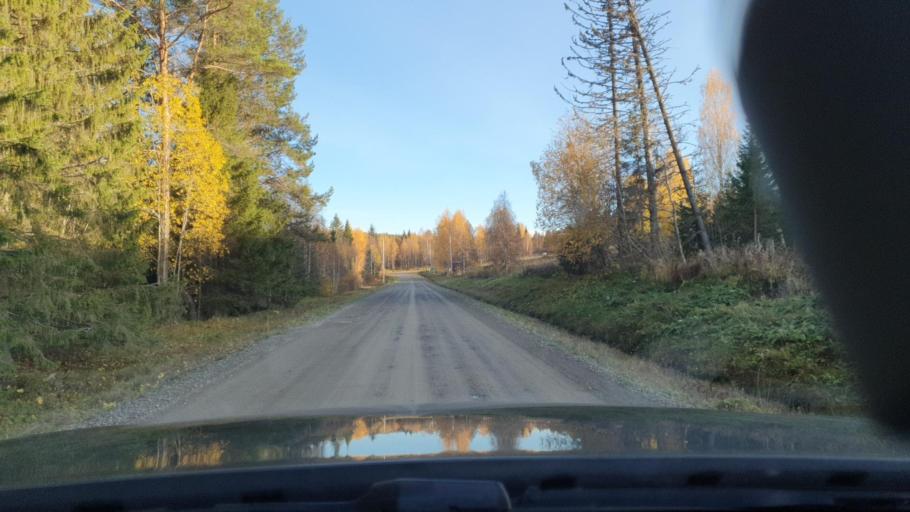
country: SE
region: Jaemtland
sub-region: Stroemsunds Kommun
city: Stroemsund
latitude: 63.5133
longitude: 15.6560
